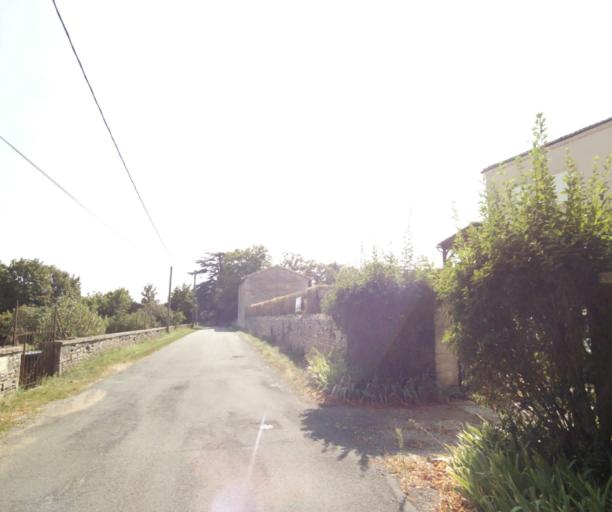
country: FR
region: Bourgogne
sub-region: Departement de Saone-et-Loire
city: Tournus
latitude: 46.5762
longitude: 4.8904
